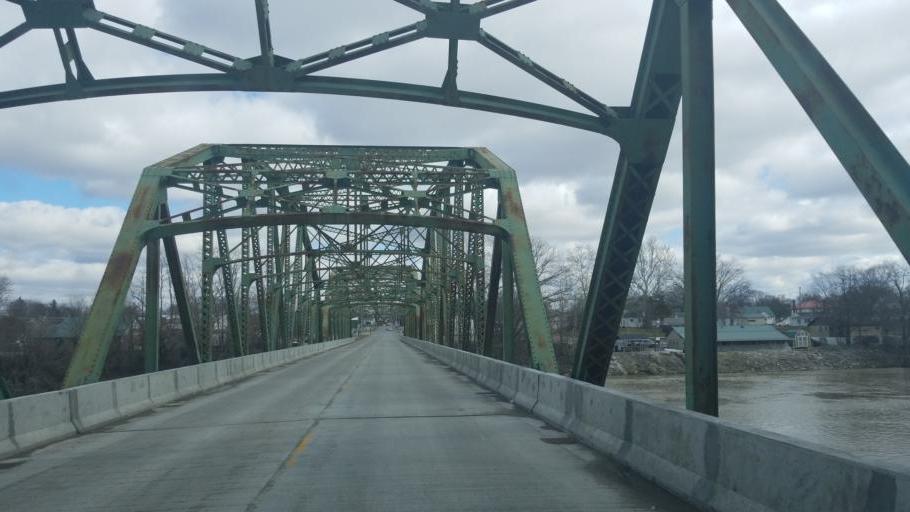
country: US
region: Indiana
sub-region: Parke County
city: Montezuma
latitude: 39.7923
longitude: -87.3755
